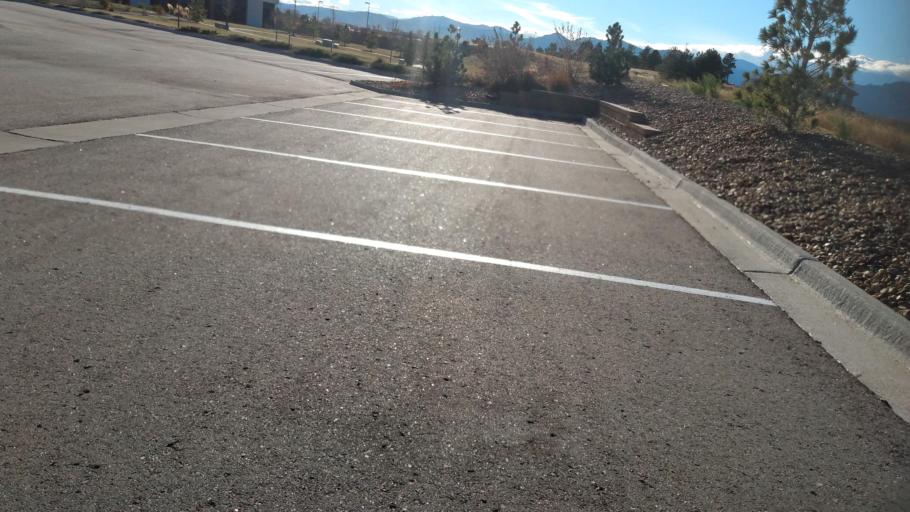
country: US
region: Colorado
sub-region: Boulder County
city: Louisville
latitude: 39.9704
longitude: -105.1219
